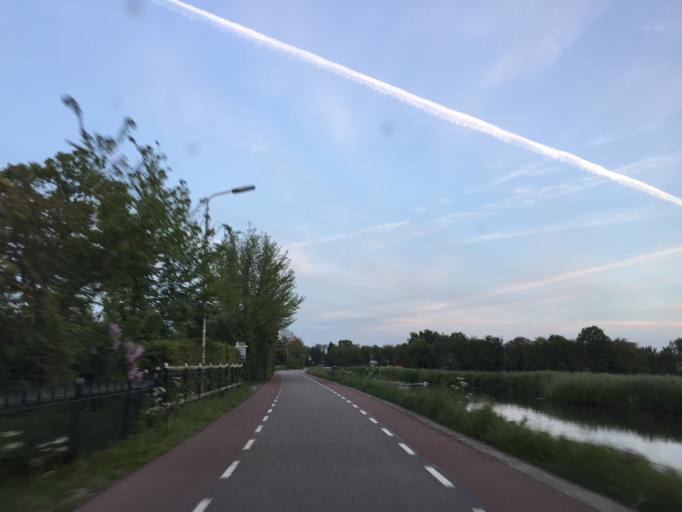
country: NL
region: South Holland
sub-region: Gemeente Pijnacker-Nootdorp
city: Pijnacker
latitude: 52.0328
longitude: 4.4295
